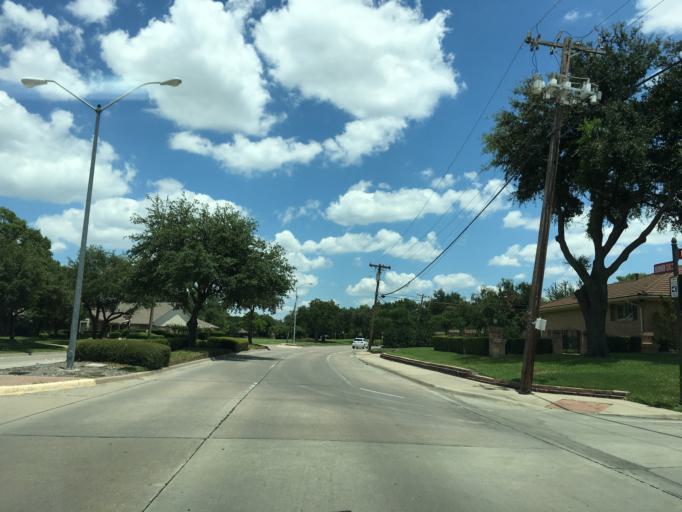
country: US
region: Texas
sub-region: Dallas County
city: Carrollton
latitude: 32.9333
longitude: -96.8599
